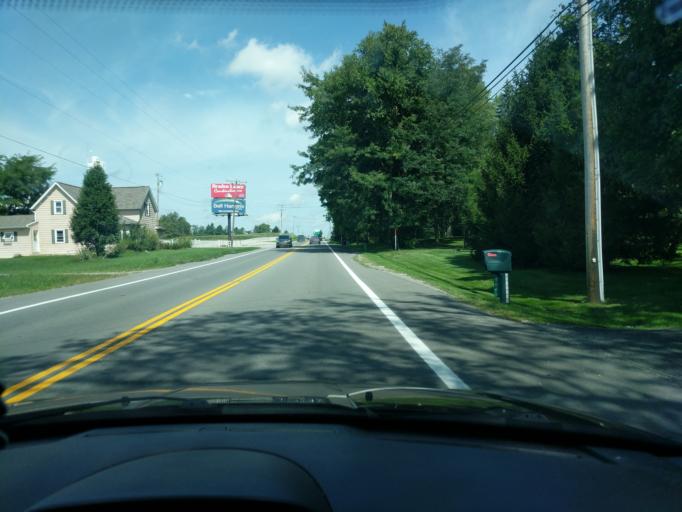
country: US
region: Ohio
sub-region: Logan County
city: West Liberty
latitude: 40.3033
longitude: -83.7594
